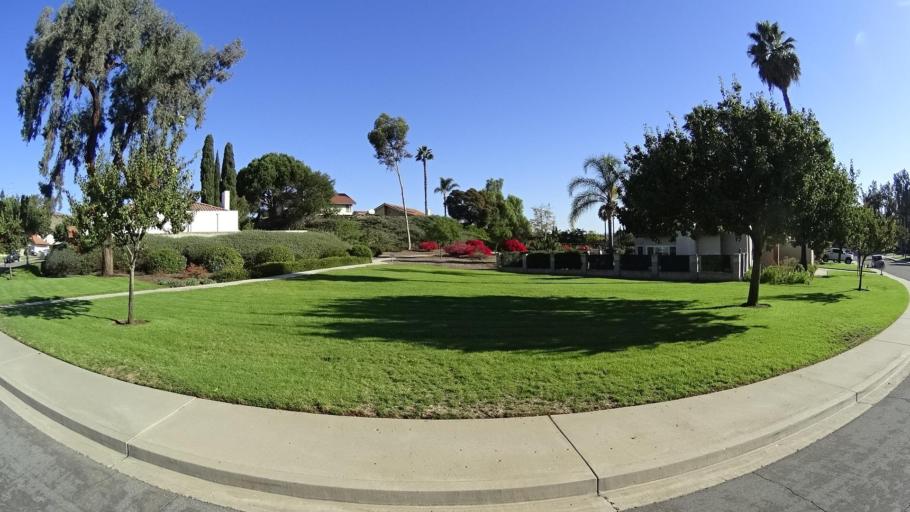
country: US
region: California
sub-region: San Diego County
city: Bonita
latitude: 32.6745
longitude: -117.0292
